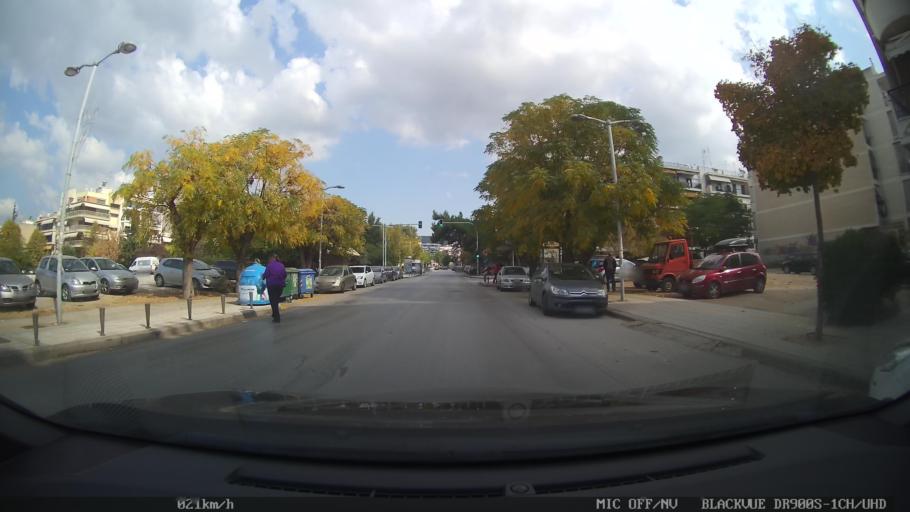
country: GR
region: Central Macedonia
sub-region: Nomos Thessalonikis
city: Triandria
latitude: 40.6082
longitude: 22.9828
